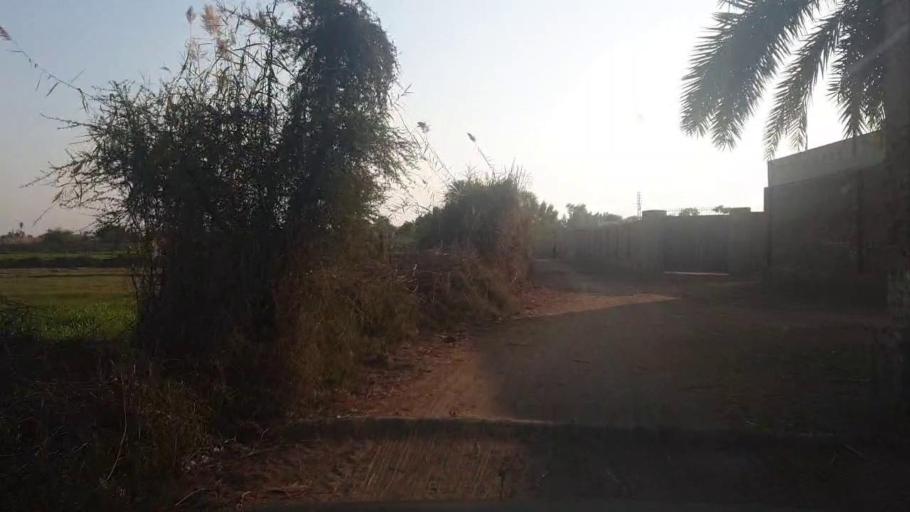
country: PK
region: Sindh
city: Sakrand
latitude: 26.0971
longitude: 68.3971
